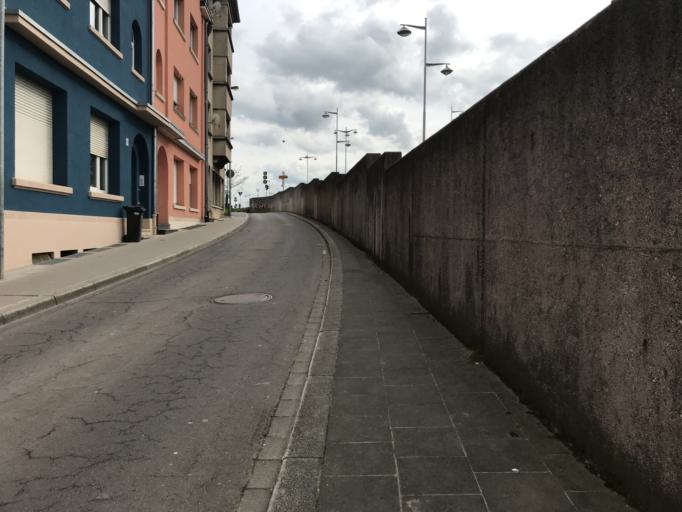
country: LU
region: Luxembourg
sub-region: Canton de Luxembourg
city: Luxembourg
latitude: 49.5964
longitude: 6.1335
